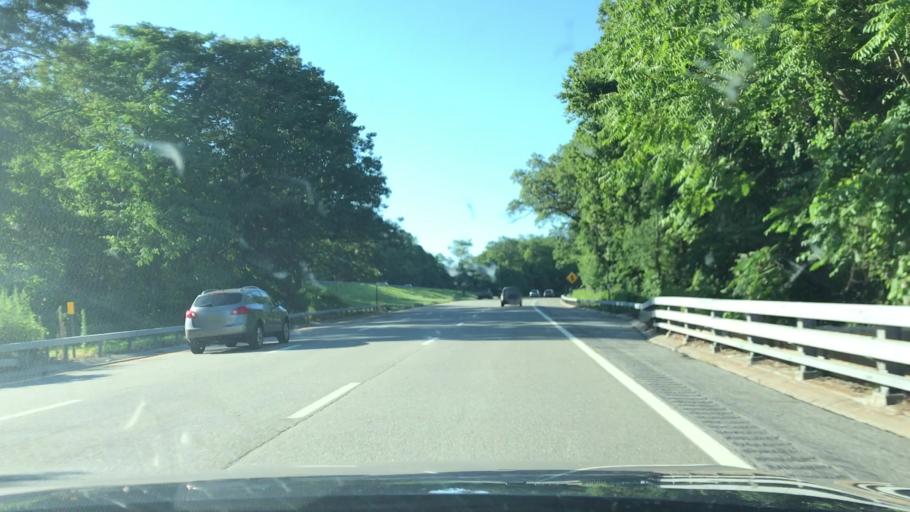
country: US
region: New York
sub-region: Westchester County
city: Yorktown Heights
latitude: 41.2148
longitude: -73.8101
